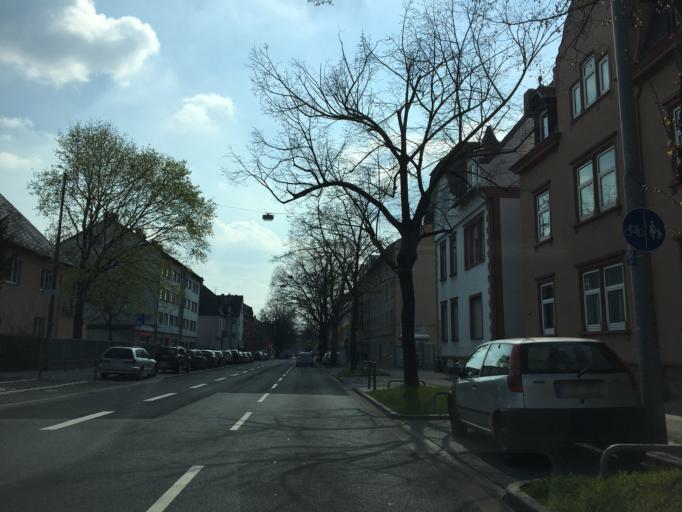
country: DE
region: Hesse
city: Sulzbach
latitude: 50.1123
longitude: 8.5366
